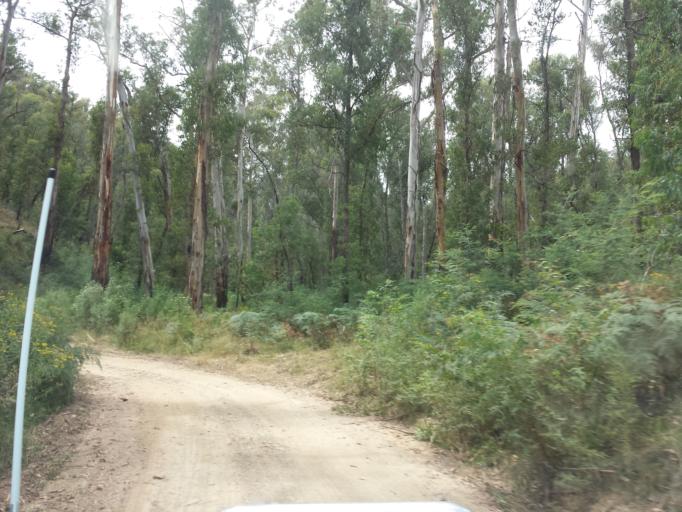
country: AU
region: Victoria
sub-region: Wellington
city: Heyfield
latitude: -37.7554
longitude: 146.4919
